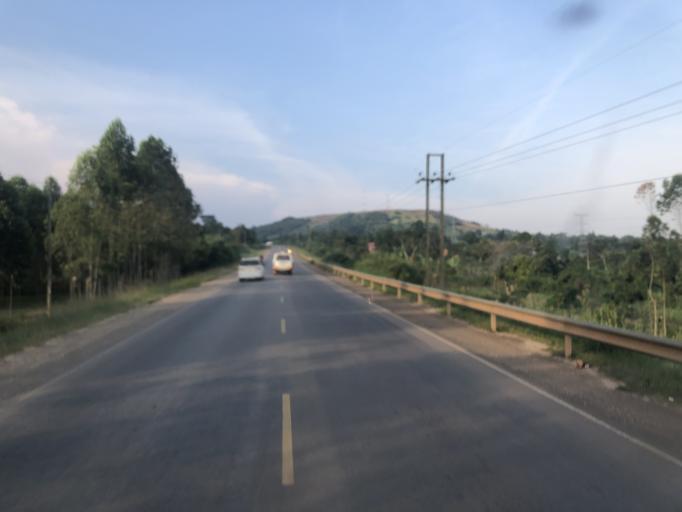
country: UG
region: Central Region
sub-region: Mpigi District
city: Mpigi
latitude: 0.1871
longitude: 32.2897
